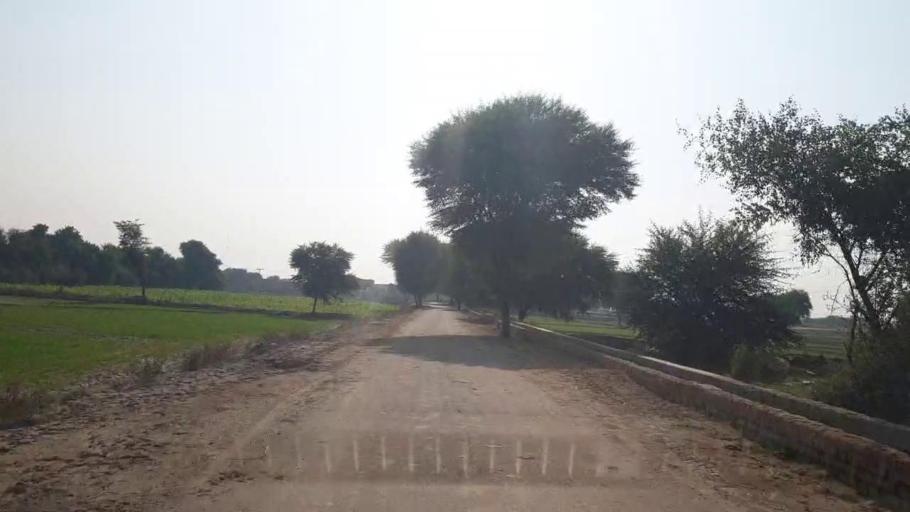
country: PK
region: Sindh
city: Sehwan
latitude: 26.4391
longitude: 67.8407
